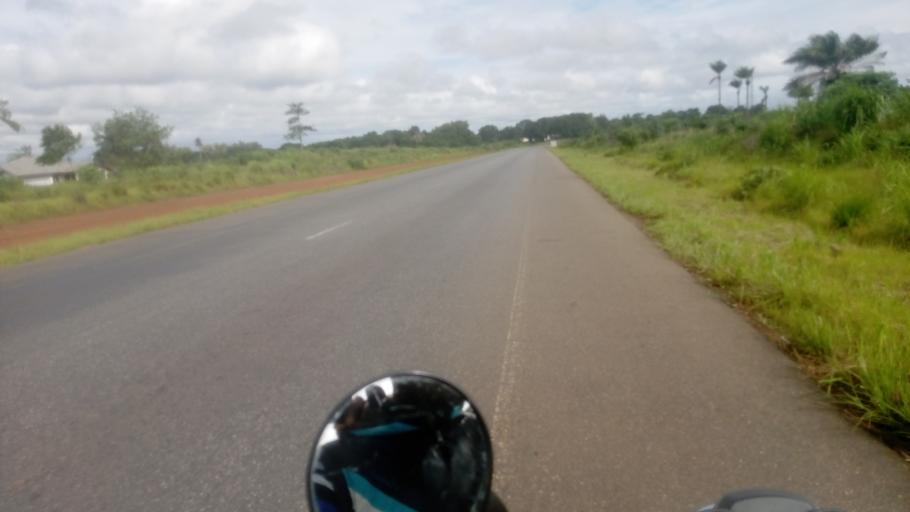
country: SL
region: Northern Province
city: Port Loko
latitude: 8.7160
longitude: -12.6812
